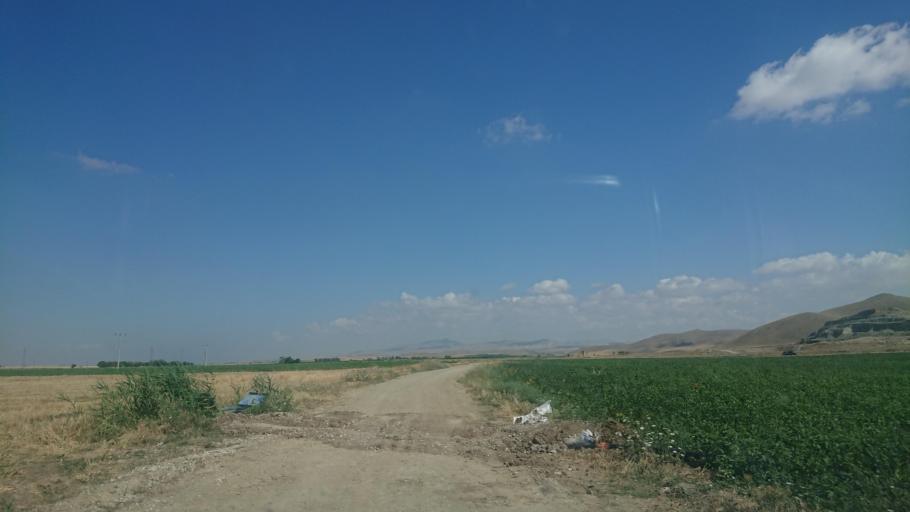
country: TR
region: Aksaray
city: Sariyahsi
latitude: 38.9772
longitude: 33.9113
